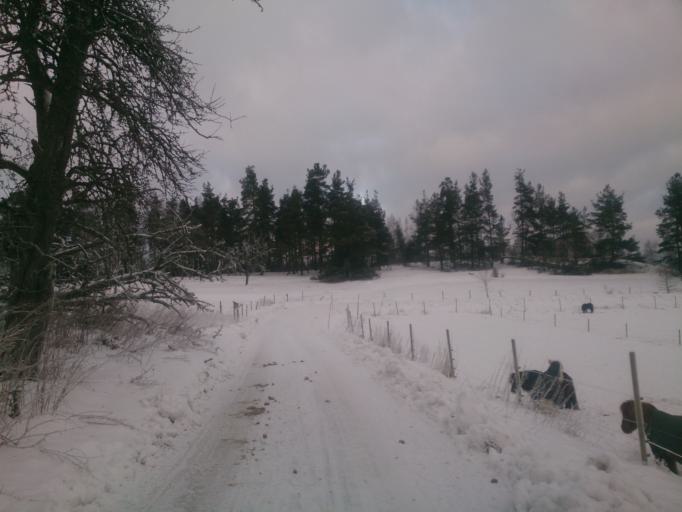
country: SE
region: OEstergoetland
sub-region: Atvidabergs Kommun
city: Atvidaberg
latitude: 58.2229
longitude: 15.9878
